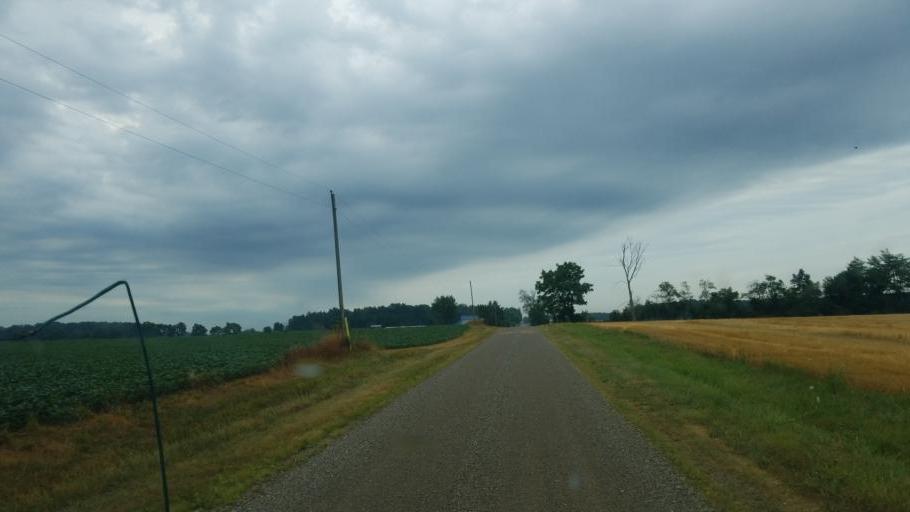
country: US
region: Indiana
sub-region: Steuben County
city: Hamilton
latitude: 41.4982
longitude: -84.9111
